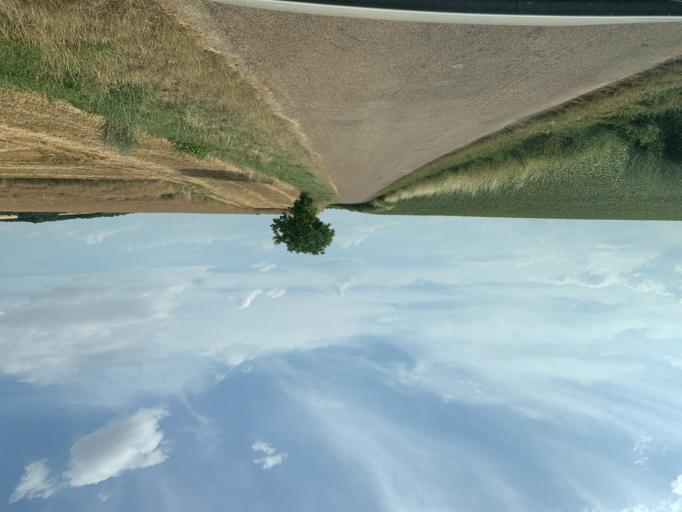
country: FR
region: Bourgogne
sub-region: Departement de l'Yonne
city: Fontenailles
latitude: 47.4738
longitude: 3.4230
